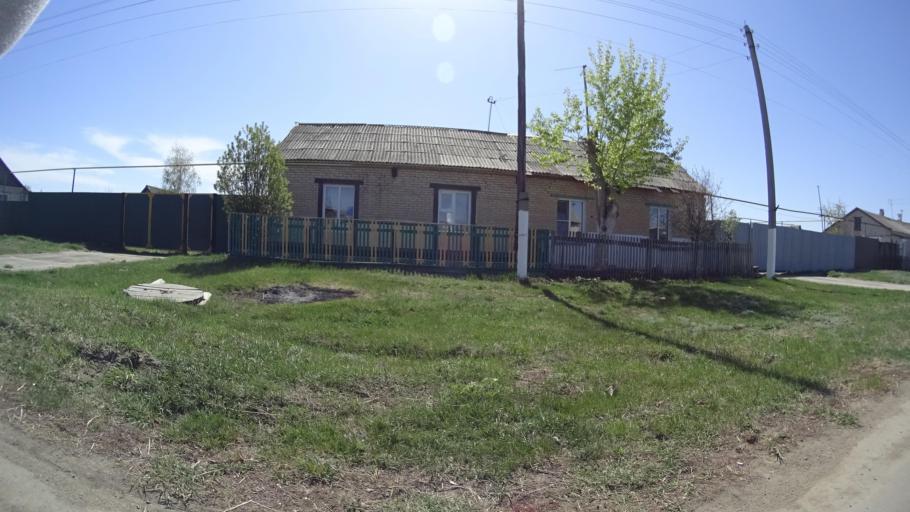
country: RU
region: Chelyabinsk
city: Chesma
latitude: 53.7945
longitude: 61.0331
